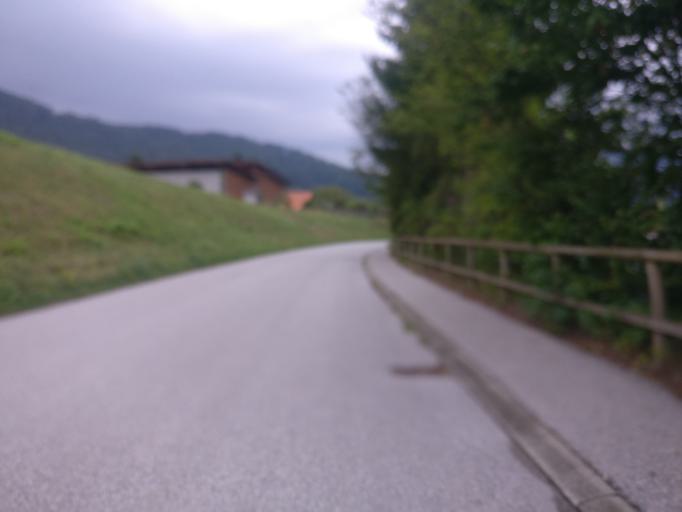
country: AT
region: Styria
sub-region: Politischer Bezirk Graz-Umgebung
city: Frohnleiten
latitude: 47.2628
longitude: 15.3146
